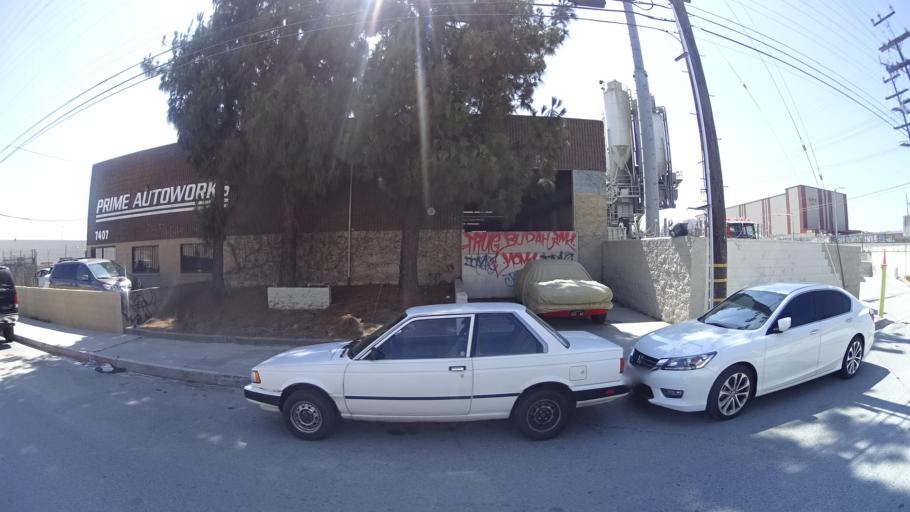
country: US
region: California
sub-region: Los Angeles County
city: Van Nuys
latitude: 34.2051
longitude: -118.4182
